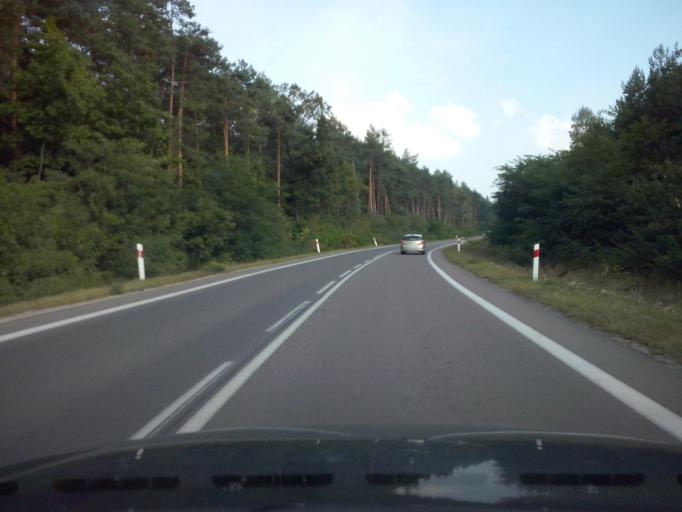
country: PL
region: Subcarpathian Voivodeship
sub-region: Powiat kolbuszowski
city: Niwiska
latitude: 50.2779
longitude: 21.5919
